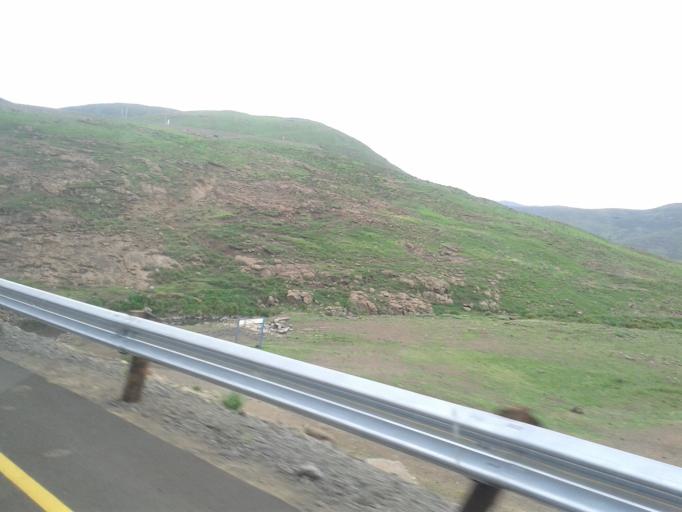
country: LS
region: Maseru
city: Nako
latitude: -29.7789
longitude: 28.0237
